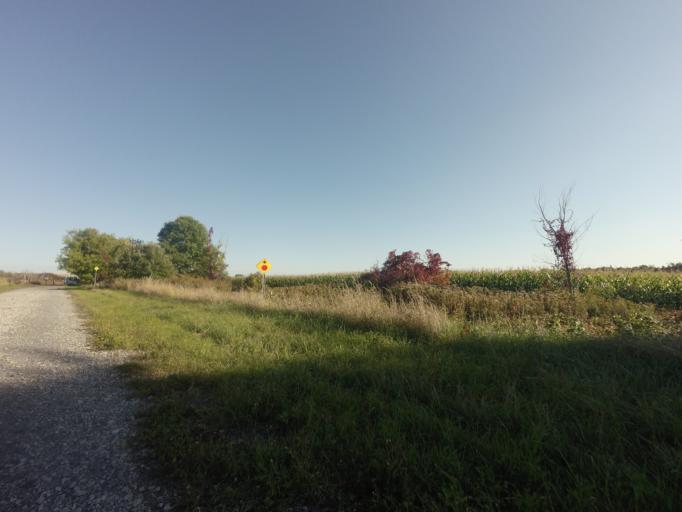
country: CA
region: Ontario
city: Hawkesbury
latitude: 45.5290
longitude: -74.5622
